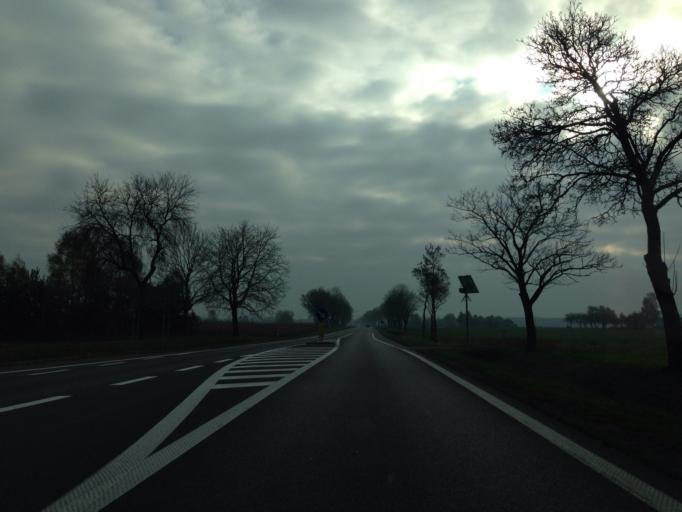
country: PL
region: Masovian Voivodeship
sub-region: Powiat sierpecki
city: Zawidz
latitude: 52.7978
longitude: 19.8624
